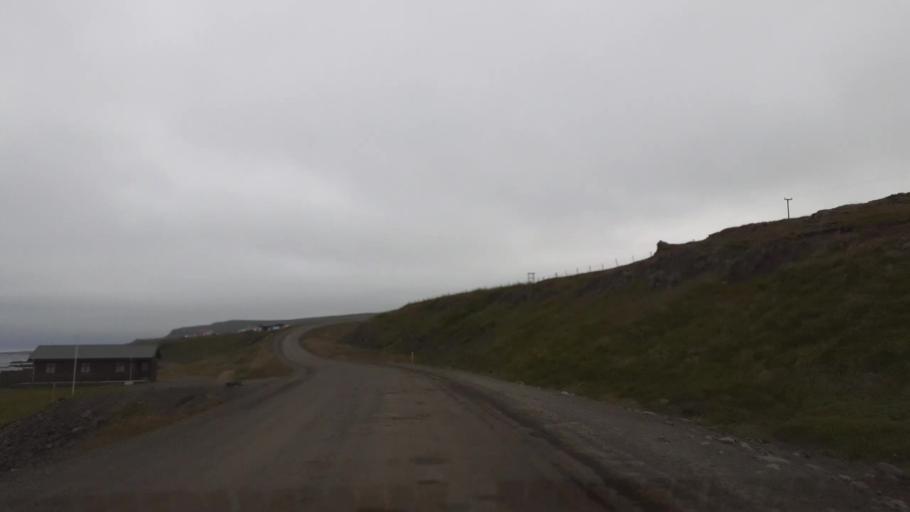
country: IS
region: Northwest
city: Saudarkrokur
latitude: 65.5279
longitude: -20.9622
